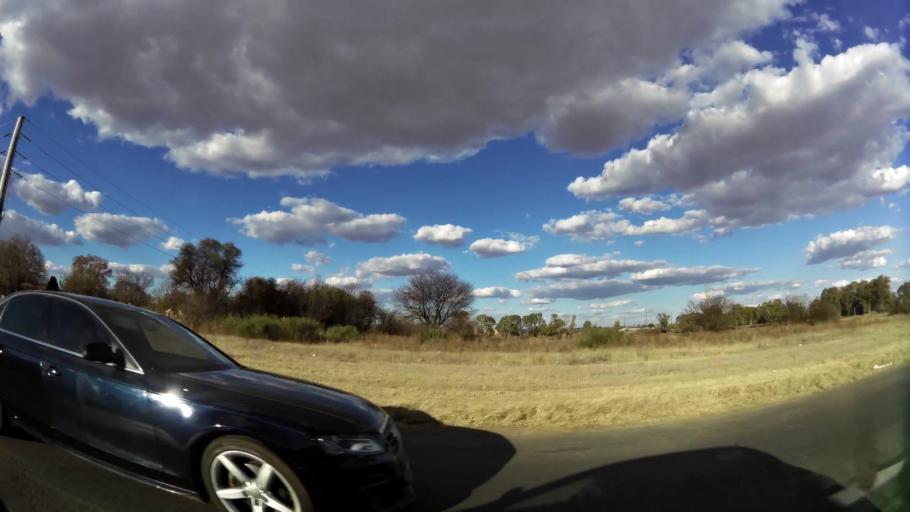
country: ZA
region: North-West
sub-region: Dr Kenneth Kaunda District Municipality
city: Potchefstroom
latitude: -26.7043
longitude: 27.0783
